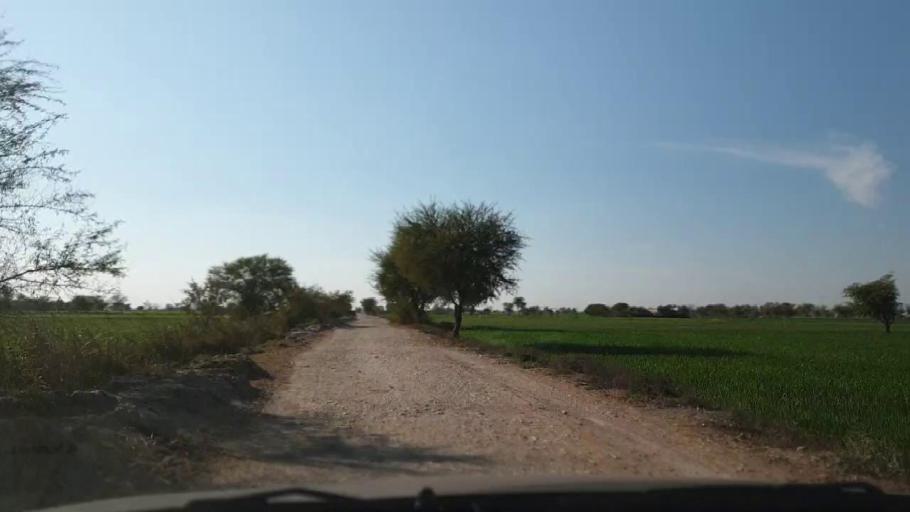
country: PK
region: Sindh
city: Khadro
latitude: 26.1554
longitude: 68.7662
